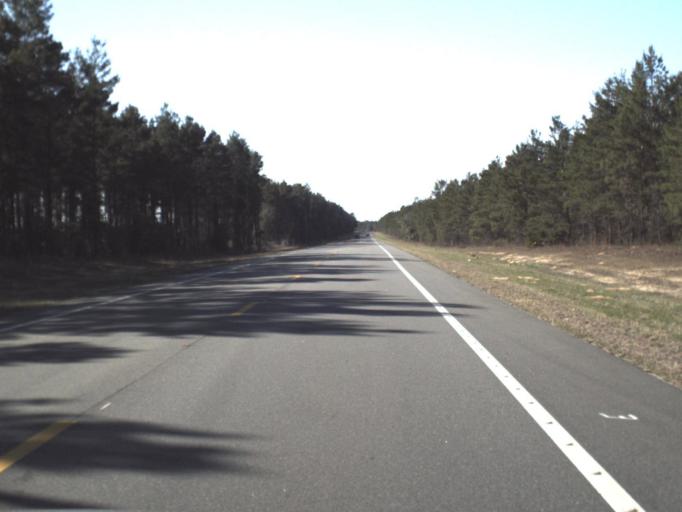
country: US
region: Florida
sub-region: Bay County
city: Youngstown
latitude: 30.4301
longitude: -85.3260
